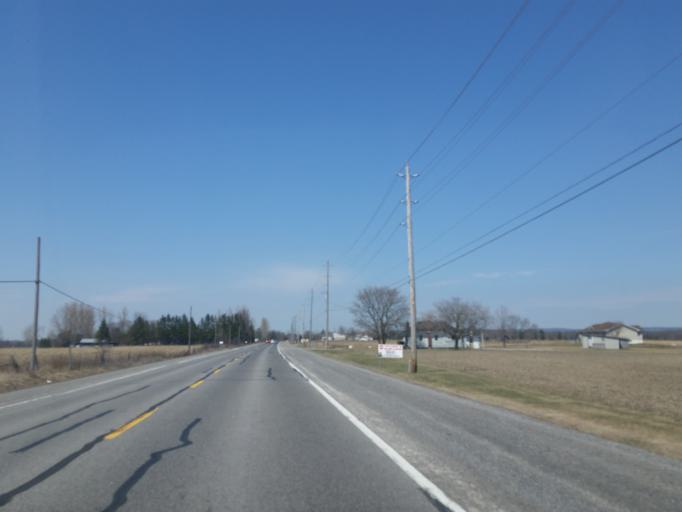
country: CA
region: Ontario
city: Bells Corners
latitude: 45.4497
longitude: -76.0588
